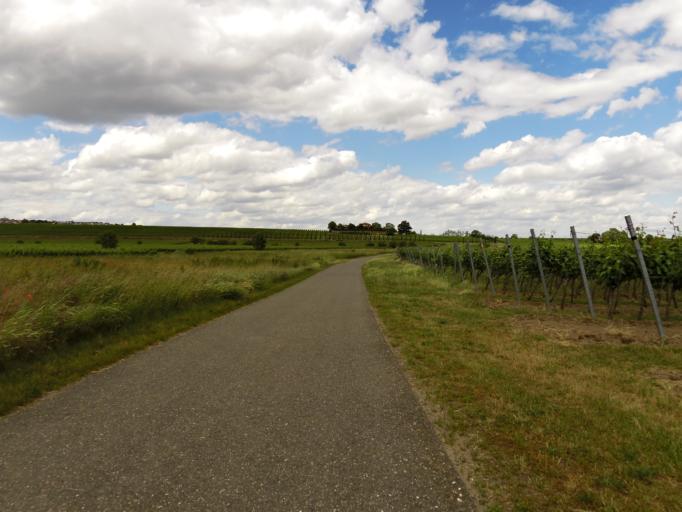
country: DE
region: Rheinland-Pfalz
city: Freinsheim
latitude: 49.5008
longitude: 8.1991
